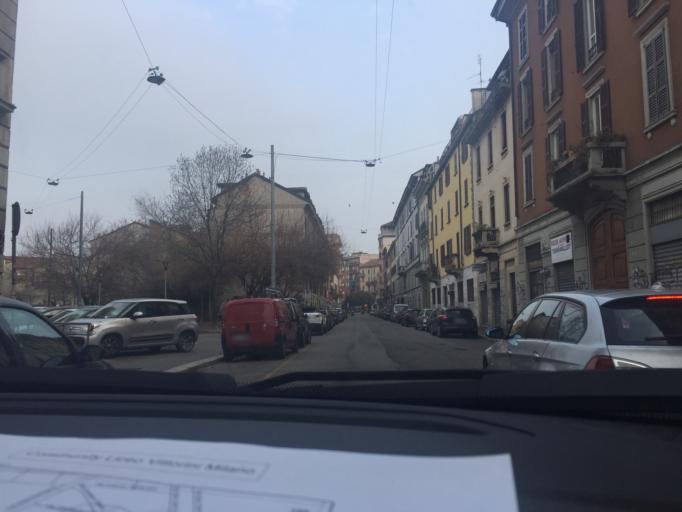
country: IT
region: Lombardy
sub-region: Citta metropolitana di Milano
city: Milano
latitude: 45.4451
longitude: 9.1775
